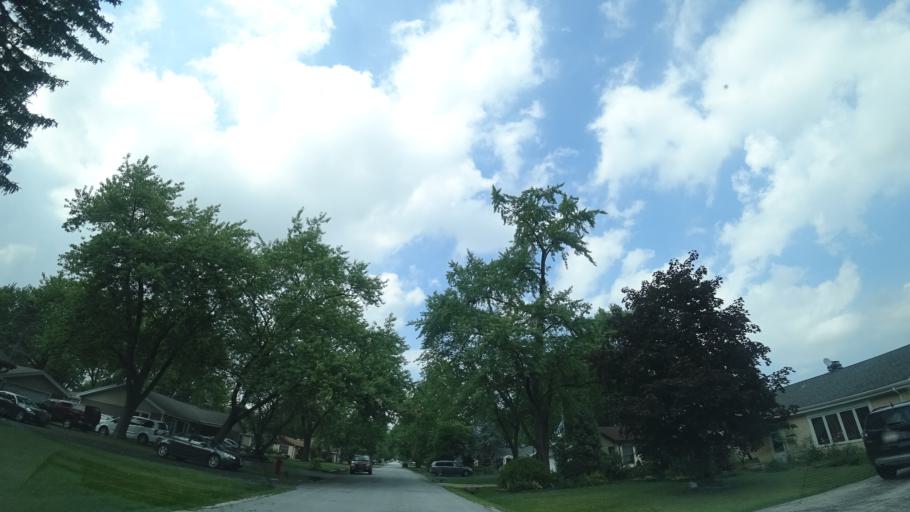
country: US
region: Illinois
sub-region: Cook County
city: Worth
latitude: 41.6813
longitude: -87.7822
